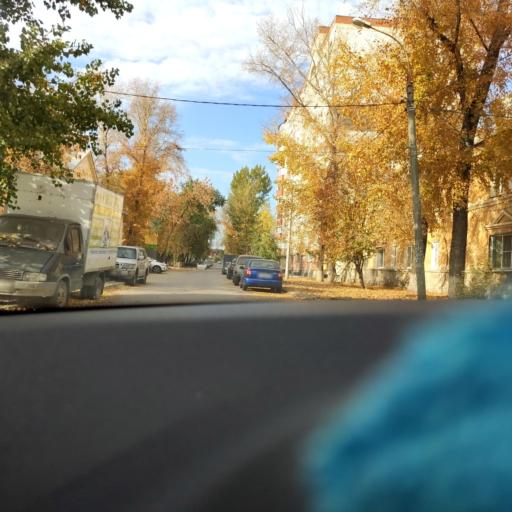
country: RU
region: Samara
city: Samara
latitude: 53.2207
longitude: 50.2537
